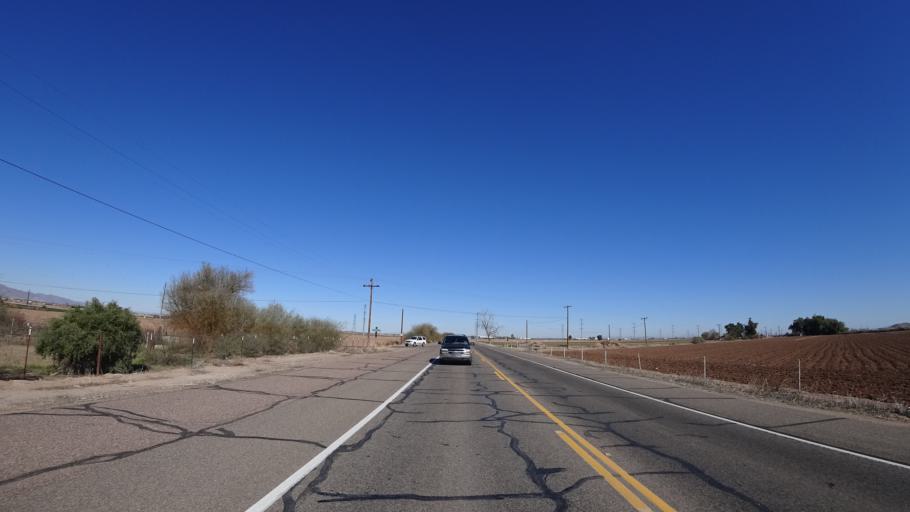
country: US
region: Arizona
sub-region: Maricopa County
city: Goodyear
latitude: 33.3916
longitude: -112.4471
